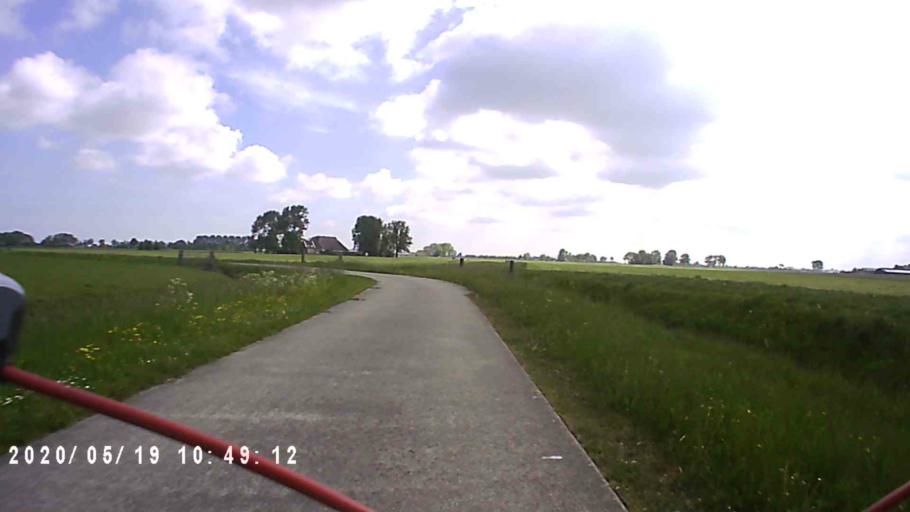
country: NL
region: Friesland
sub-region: Gemeente Kollumerland en Nieuwkruisland
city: Kollum
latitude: 53.2872
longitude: 6.2264
